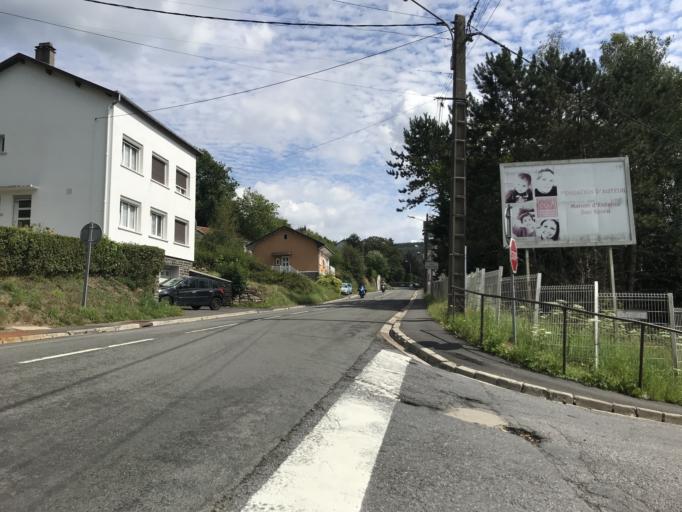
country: FR
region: Champagne-Ardenne
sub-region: Departement des Ardennes
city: Montherme
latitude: 49.8871
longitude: 4.7439
